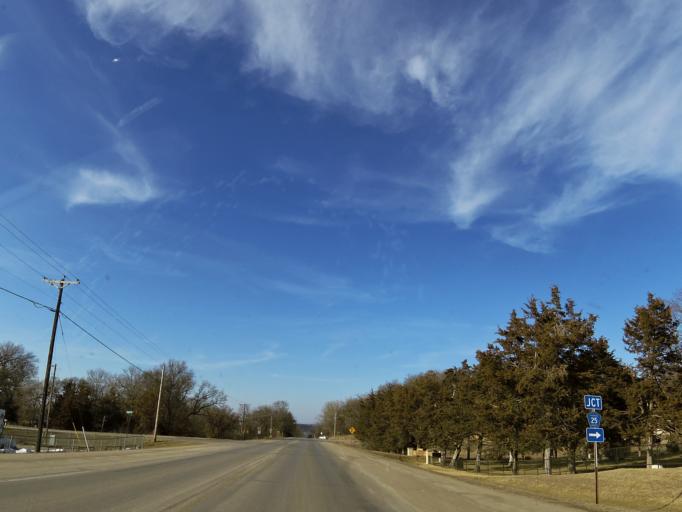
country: US
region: Minnesota
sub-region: Goodhue County
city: Cannon Falls
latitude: 44.4980
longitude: -92.9057
